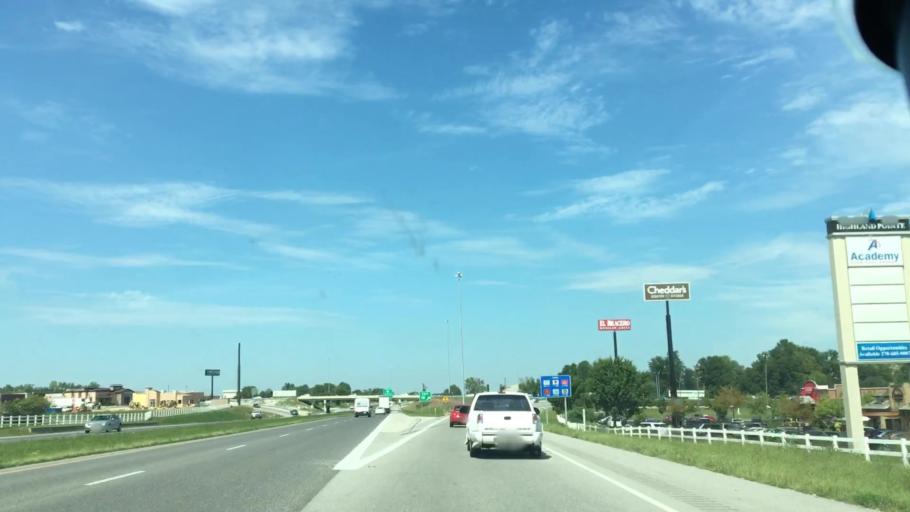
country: US
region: Kentucky
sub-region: Daviess County
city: Owensboro
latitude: 37.7539
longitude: -87.0712
